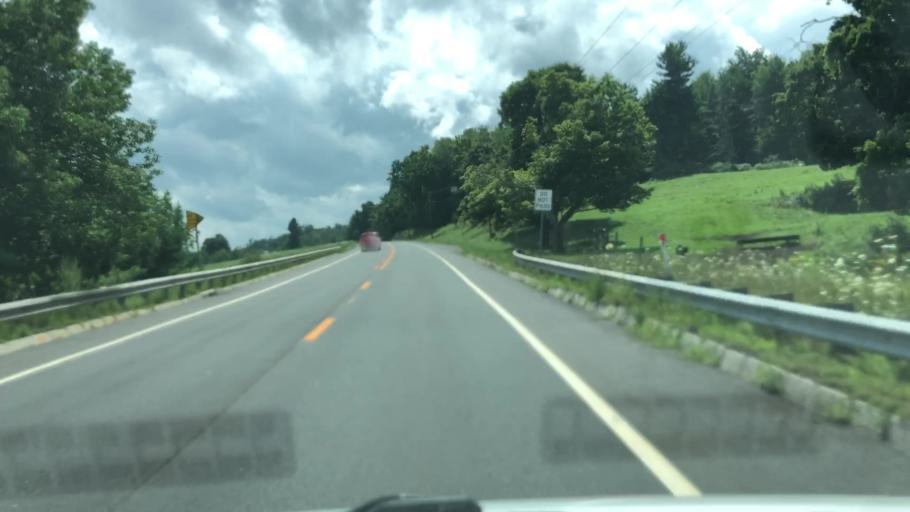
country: US
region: Massachusetts
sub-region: Franklin County
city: Ashfield
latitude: 42.5244
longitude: -72.8072
